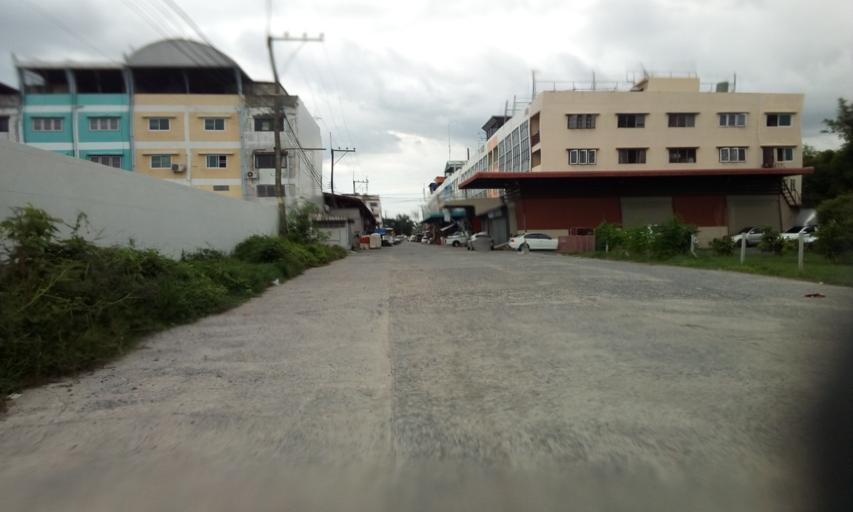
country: TH
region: Pathum Thani
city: Nong Suea
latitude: 14.0593
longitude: 100.8355
